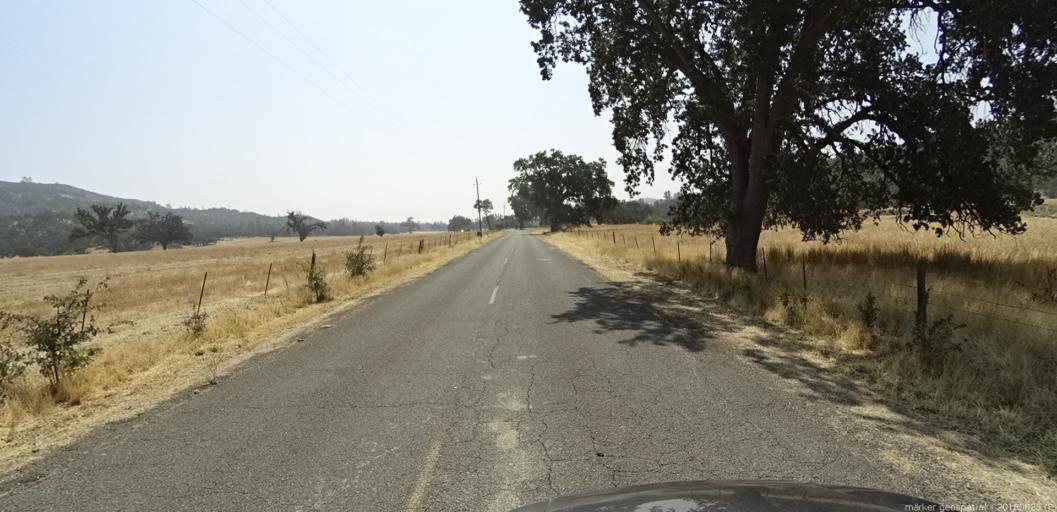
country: US
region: California
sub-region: Fresno County
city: Coalinga
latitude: 35.9256
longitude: -120.5009
